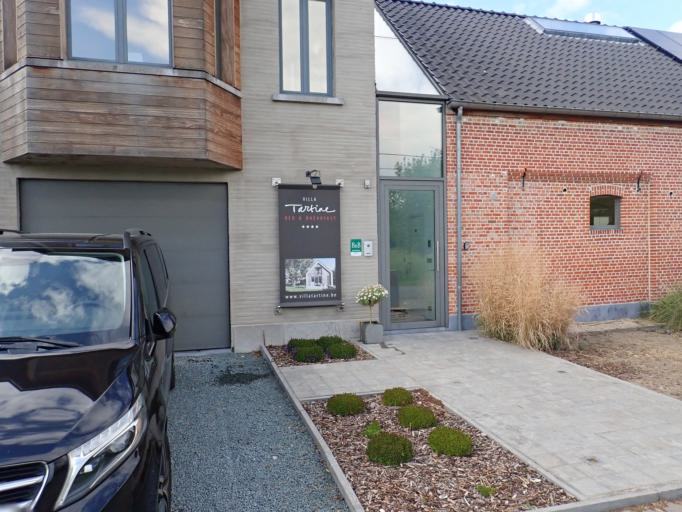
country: BE
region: Flanders
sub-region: Provincie Antwerpen
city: Puurs
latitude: 51.0633
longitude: 4.2651
